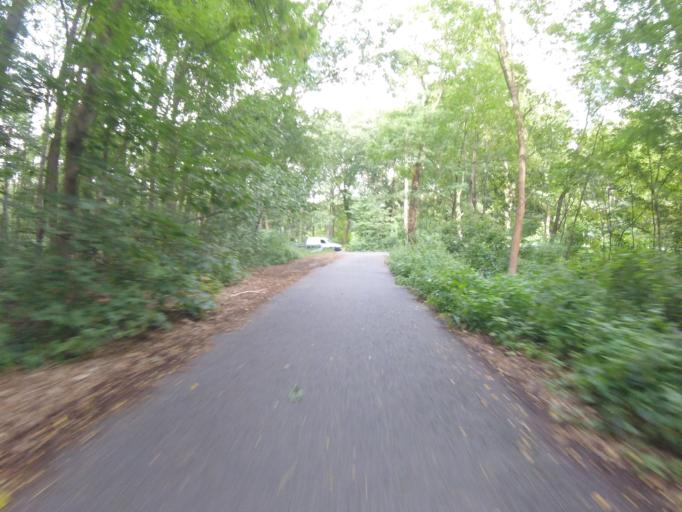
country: DE
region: Brandenburg
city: Halbe
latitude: 52.1116
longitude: 13.7580
